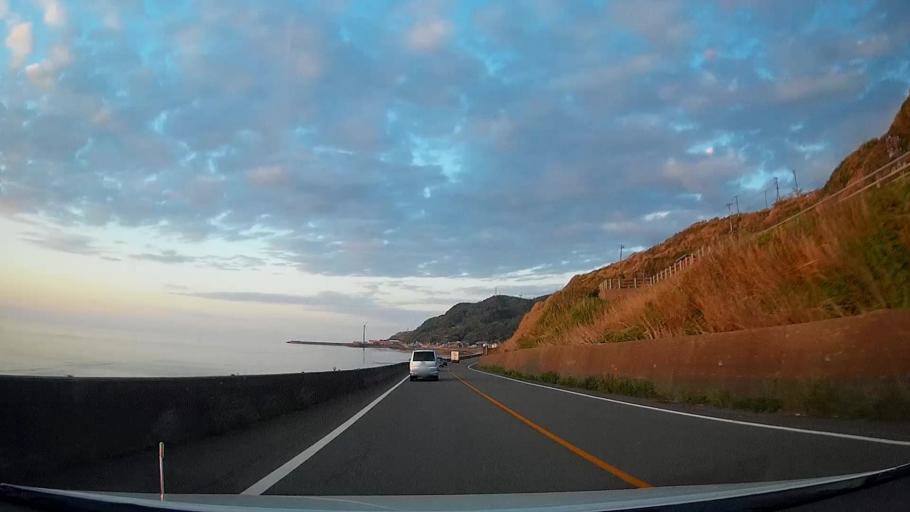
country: JP
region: Niigata
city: Joetsu
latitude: 37.1525
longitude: 138.0750
